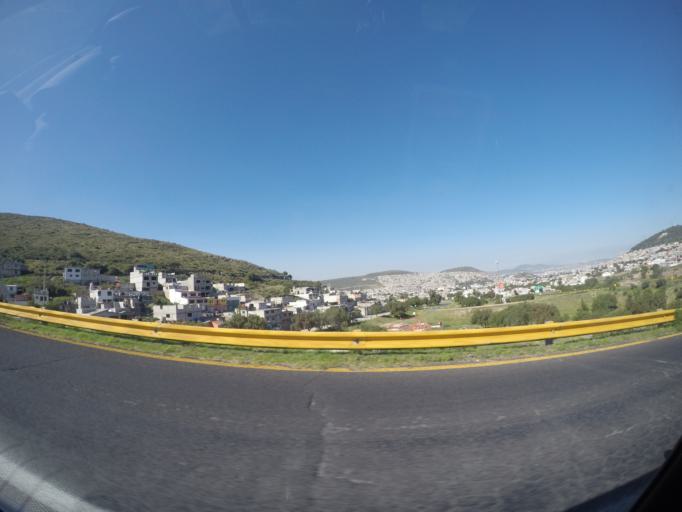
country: MX
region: Hidalgo
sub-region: Mineral de la Reforma
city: Rio de la Soledad
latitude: 20.1194
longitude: -98.7086
